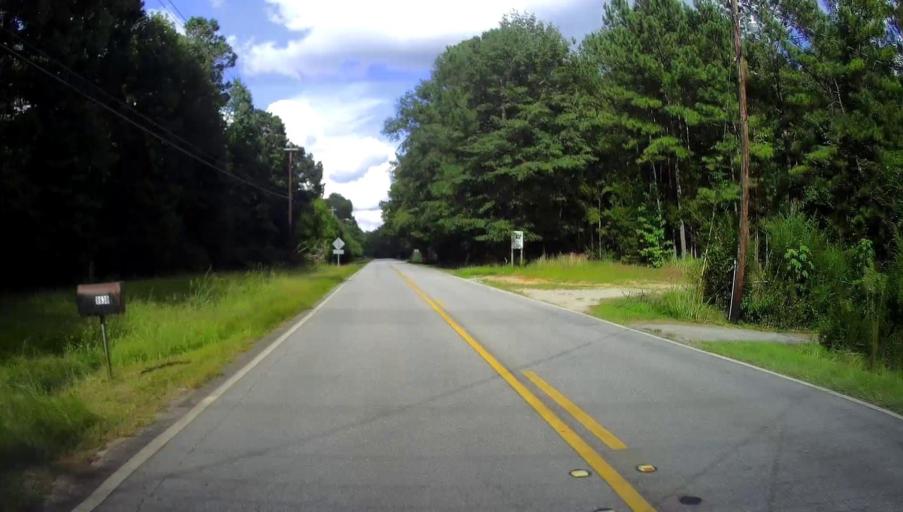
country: US
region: Georgia
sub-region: Muscogee County
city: Columbus
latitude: 32.5686
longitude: -84.8372
